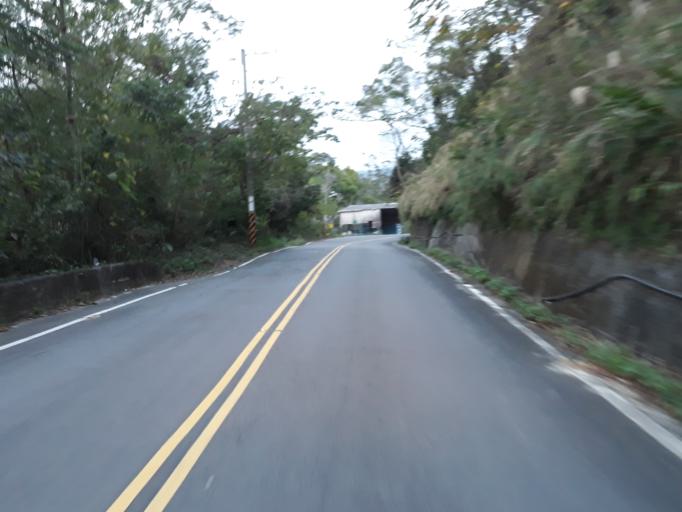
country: TW
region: Taiwan
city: Fengyuan
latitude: 24.3680
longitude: 120.8673
